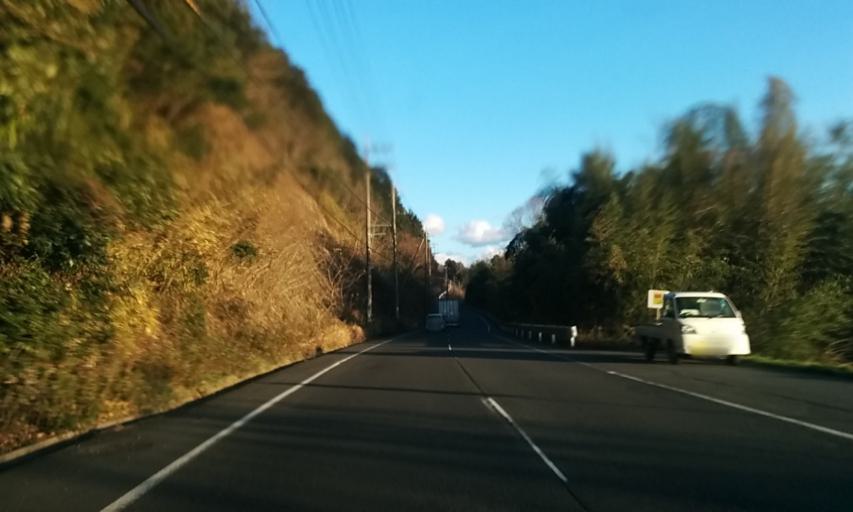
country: JP
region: Kyoto
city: Ayabe
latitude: 35.3101
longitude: 135.2633
